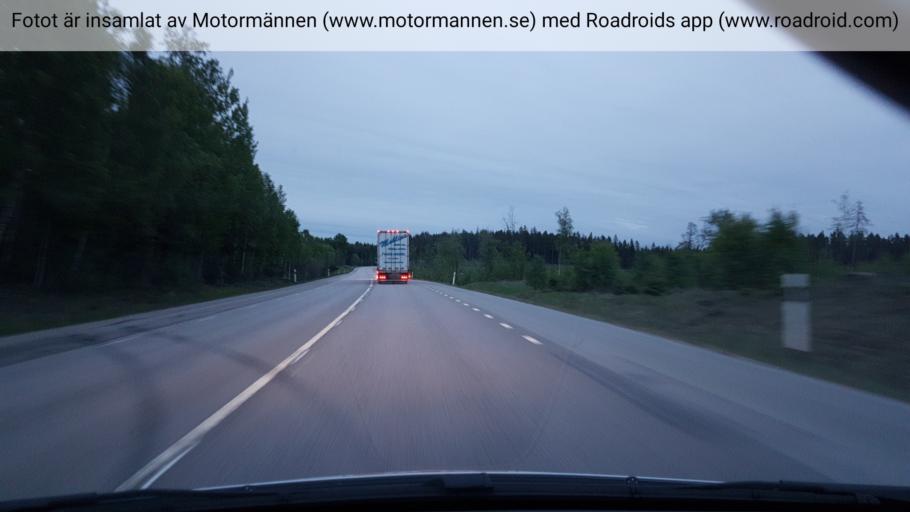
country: SE
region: Uppsala
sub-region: Heby Kommun
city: Heby
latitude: 59.9364
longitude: 16.8071
